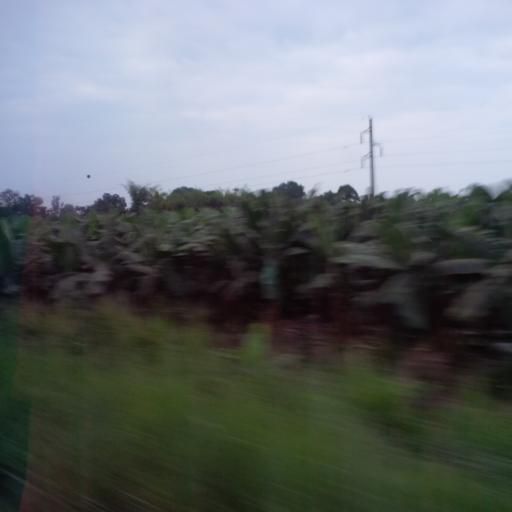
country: EC
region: Canar
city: La Troncal
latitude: -2.3437
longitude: -79.3725
